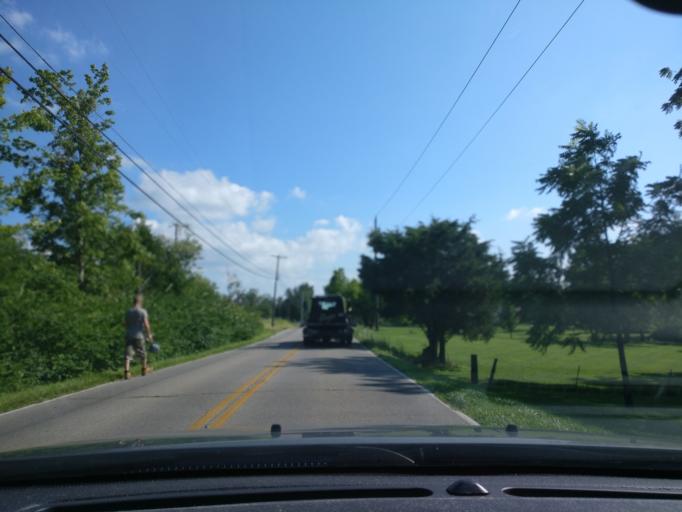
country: US
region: Ohio
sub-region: Warren County
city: Springboro
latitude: 39.5860
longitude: -84.2486
